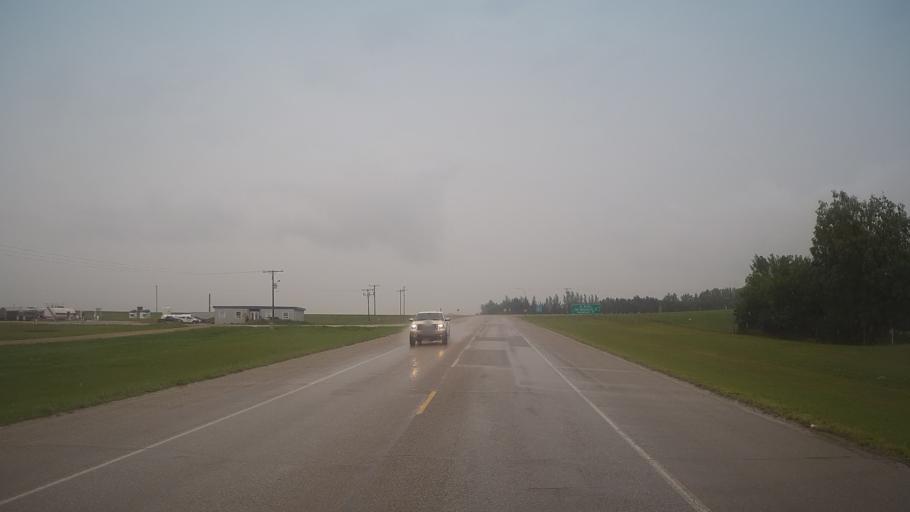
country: CA
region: Saskatchewan
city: Biggar
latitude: 52.0626
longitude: -107.9966
